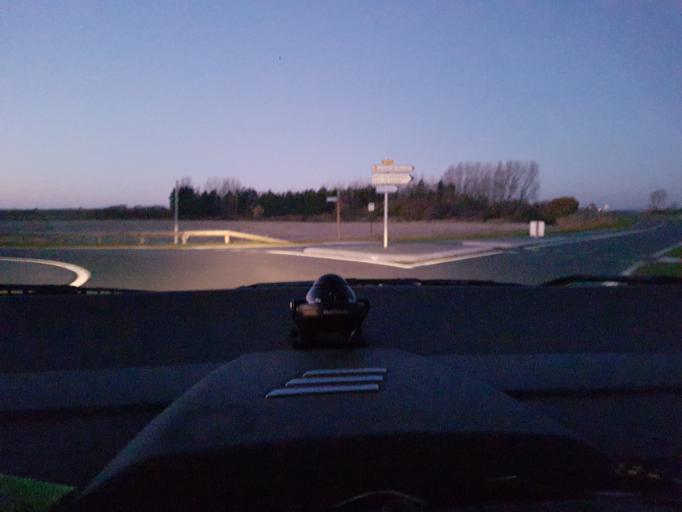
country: FR
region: Picardie
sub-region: Departement de la Somme
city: Pende
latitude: 50.1997
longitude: 1.5542
